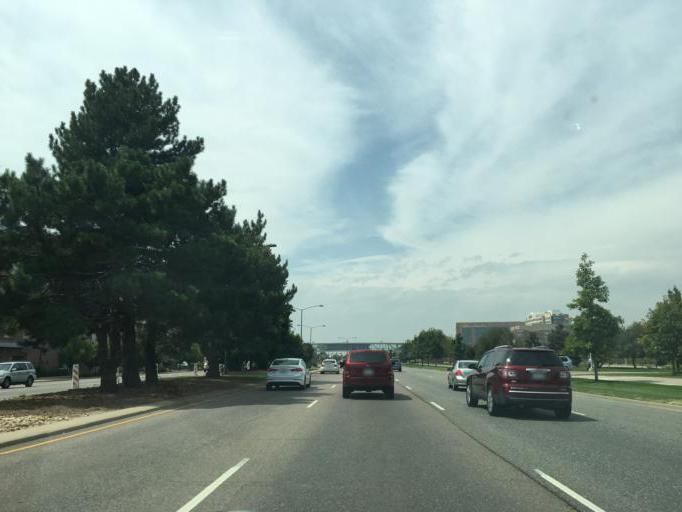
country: US
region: Colorado
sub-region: Adams County
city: Aurora
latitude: 39.7403
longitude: -104.8323
